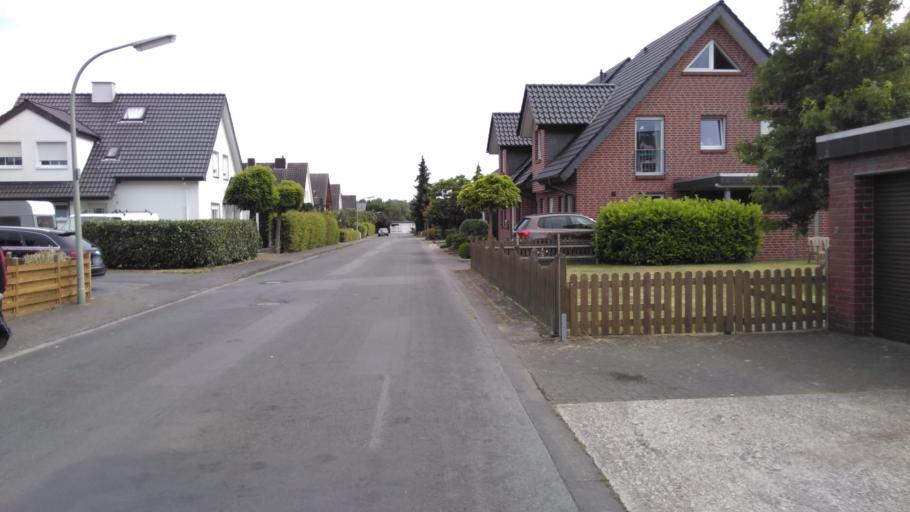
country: DE
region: North Rhine-Westphalia
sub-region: Regierungsbezirk Detmold
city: Verl
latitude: 51.8737
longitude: 8.5067
